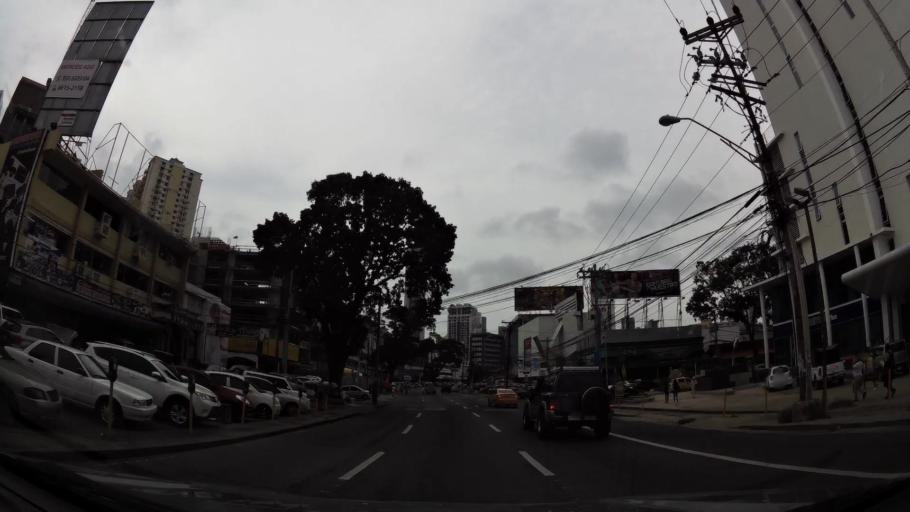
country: PA
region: Panama
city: Panama
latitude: 8.9882
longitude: -79.5230
